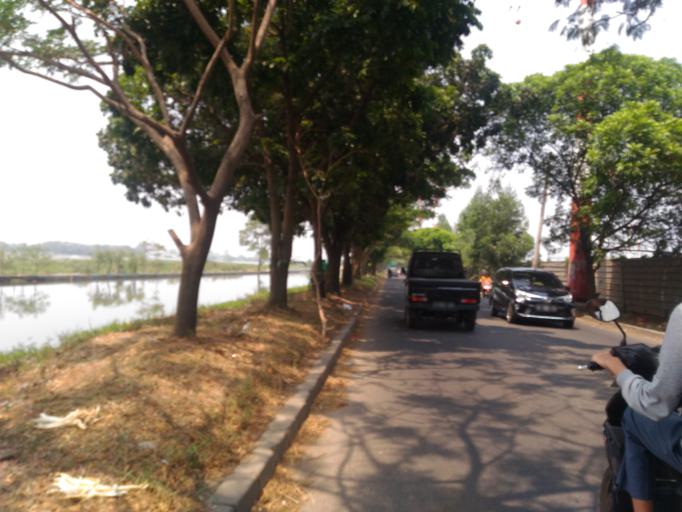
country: ID
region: Banten
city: Tangerang
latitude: -6.1535
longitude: 106.6052
